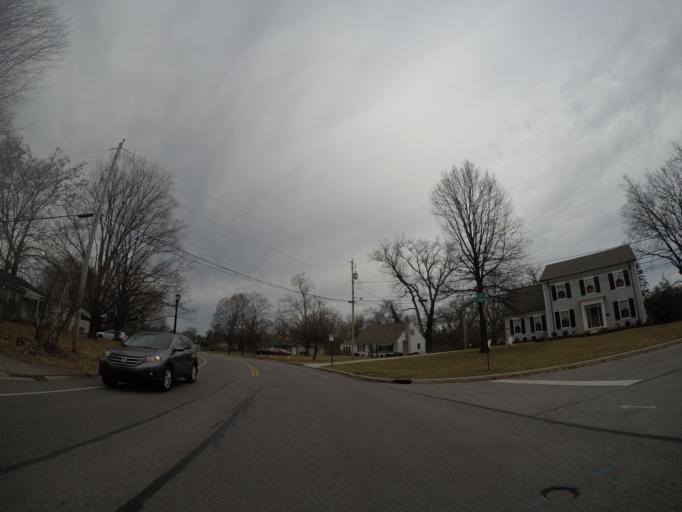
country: US
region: Ohio
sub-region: Franklin County
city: Upper Arlington
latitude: 40.0289
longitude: -83.0845
